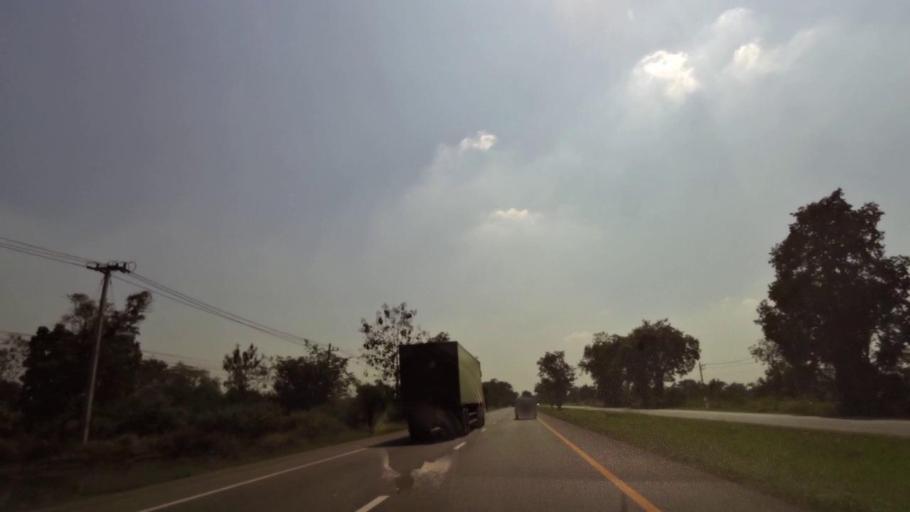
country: TH
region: Phichit
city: Bueng Na Rang
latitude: 16.2281
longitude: 100.1260
